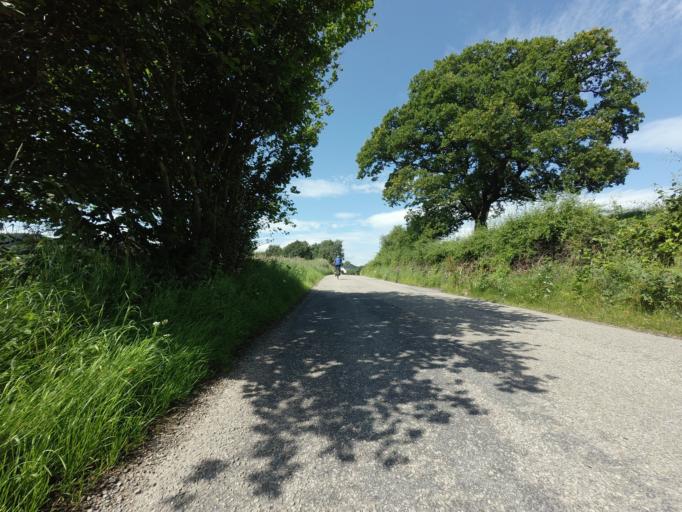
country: GB
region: Scotland
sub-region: Highland
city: Inverness
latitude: 57.5228
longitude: -4.3111
